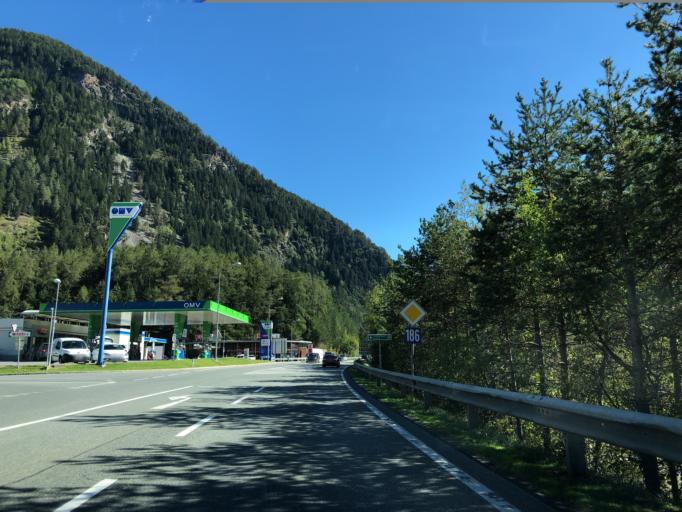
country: AT
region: Tyrol
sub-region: Politischer Bezirk Imst
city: Sautens
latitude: 47.2299
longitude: 10.8558
